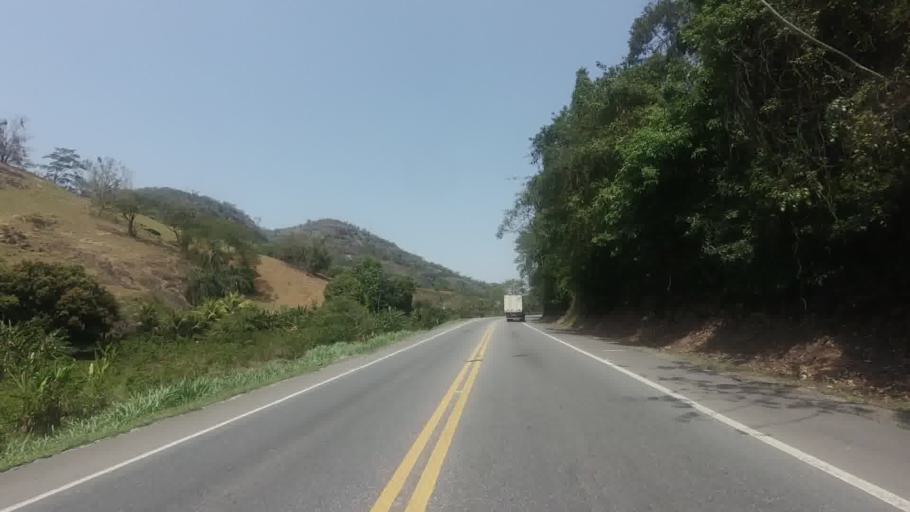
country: BR
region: Espirito Santo
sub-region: Rio Novo Do Sul
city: Rio Novo do Sul
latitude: -20.8404
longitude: -40.8717
